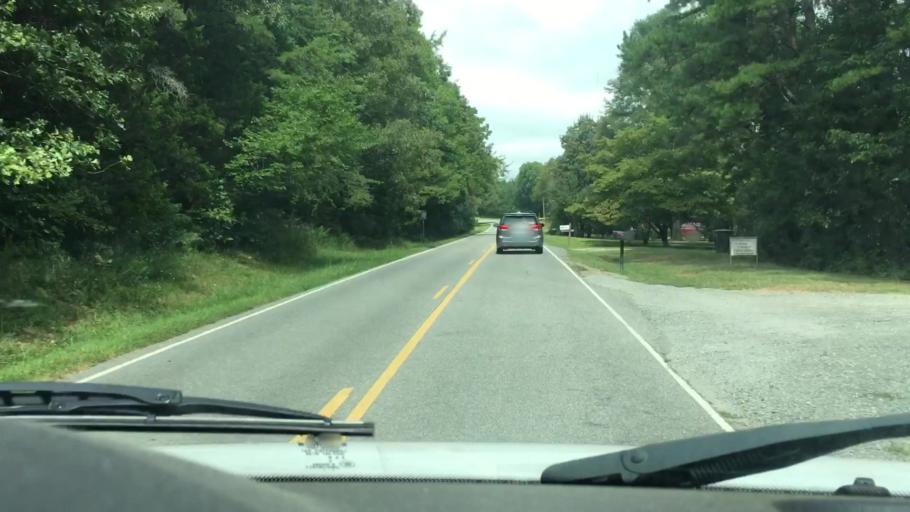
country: US
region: North Carolina
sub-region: Gaston County
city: Davidson
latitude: 35.5127
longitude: -80.7988
